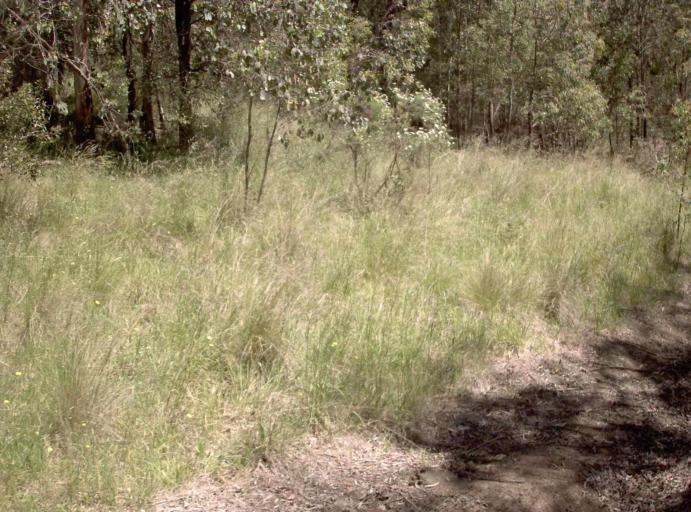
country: AU
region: Victoria
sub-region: East Gippsland
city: Lakes Entrance
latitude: -37.2378
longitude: 148.2588
